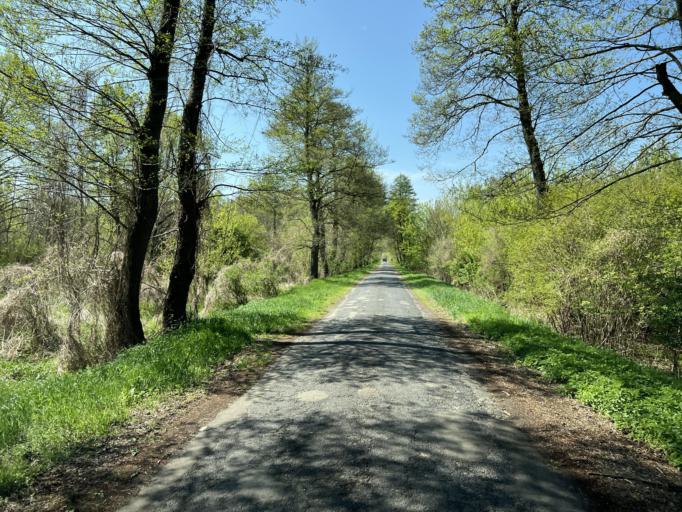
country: HU
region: Pest
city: Inarcs
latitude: 47.2594
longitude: 19.2883
